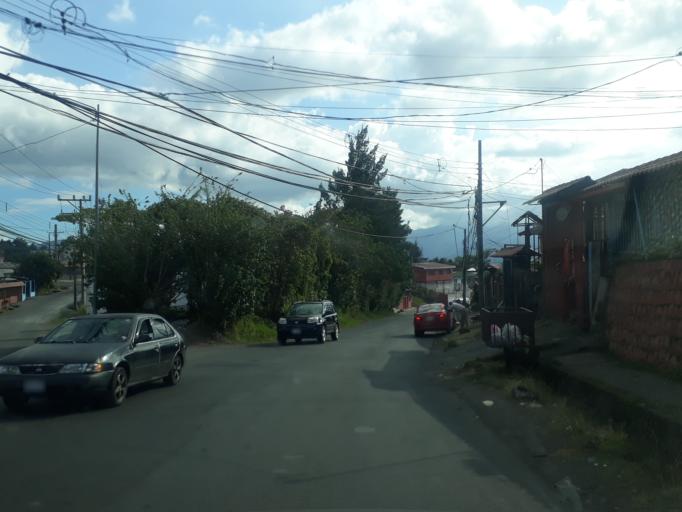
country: CR
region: San Jose
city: Ipis
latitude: 9.9816
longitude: -84.0303
